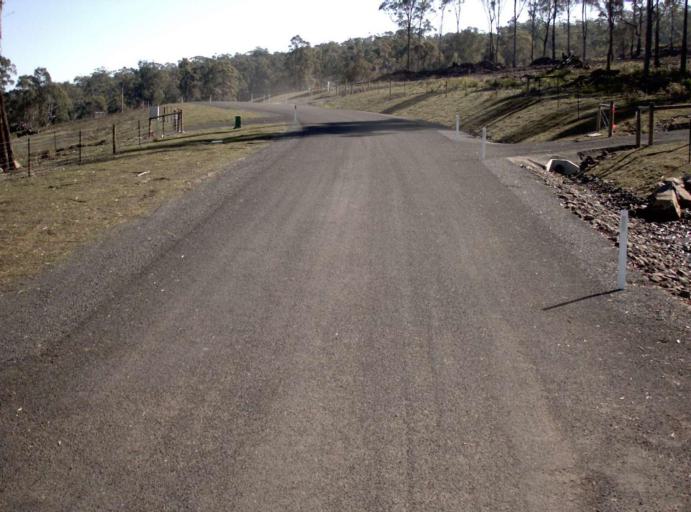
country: AU
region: Tasmania
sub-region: Launceston
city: Mayfield
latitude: -41.2819
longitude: 147.0290
